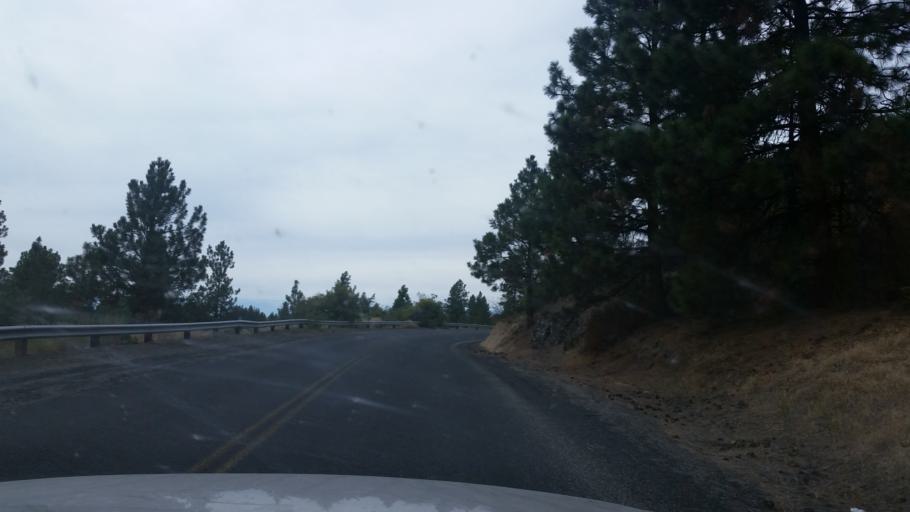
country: US
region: Washington
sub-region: Spokane County
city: Spokane
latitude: 47.6548
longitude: -117.4844
